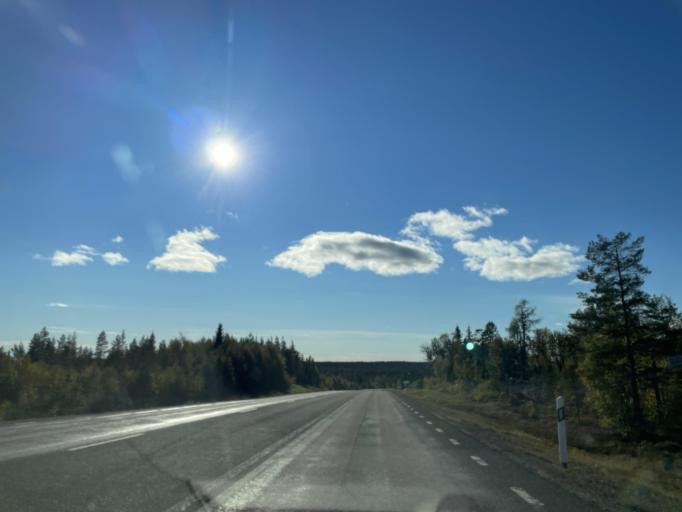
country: SE
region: Dalarna
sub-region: Malung-Saelens kommun
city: Malung
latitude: 60.5152
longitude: 13.4926
